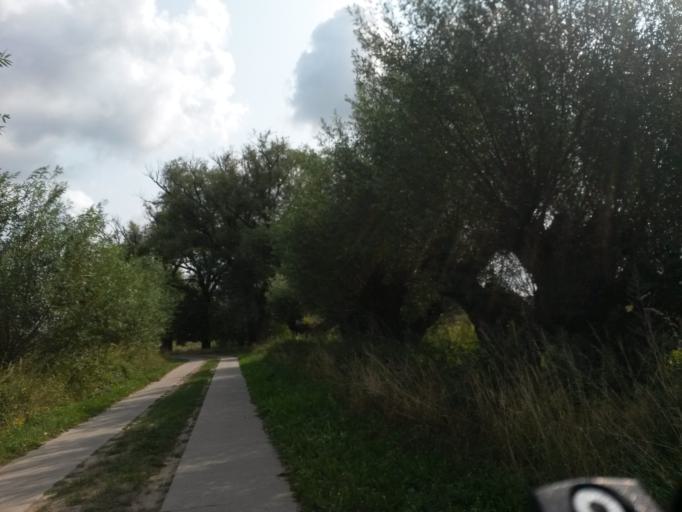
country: DE
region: Saxony-Anhalt
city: Arneburg
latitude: 52.6470
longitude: 12.0373
